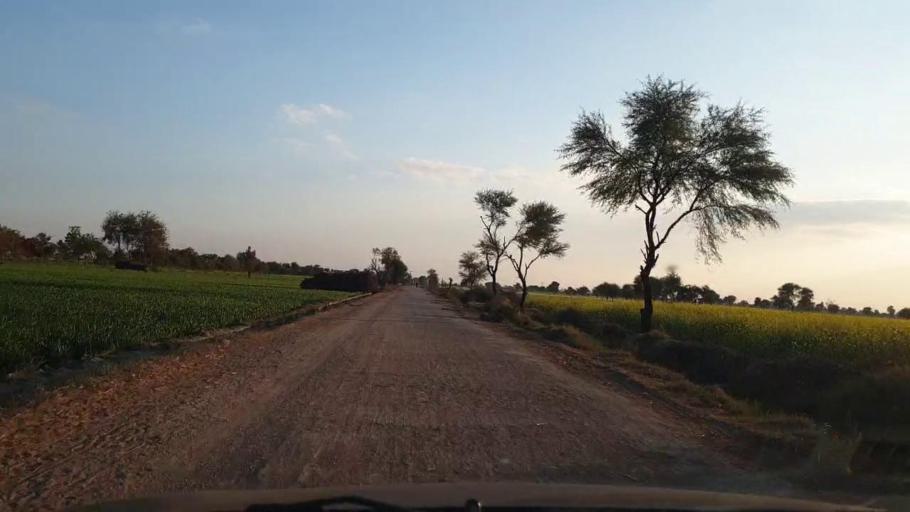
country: PK
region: Sindh
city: Sinjhoro
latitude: 26.0015
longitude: 68.8014
